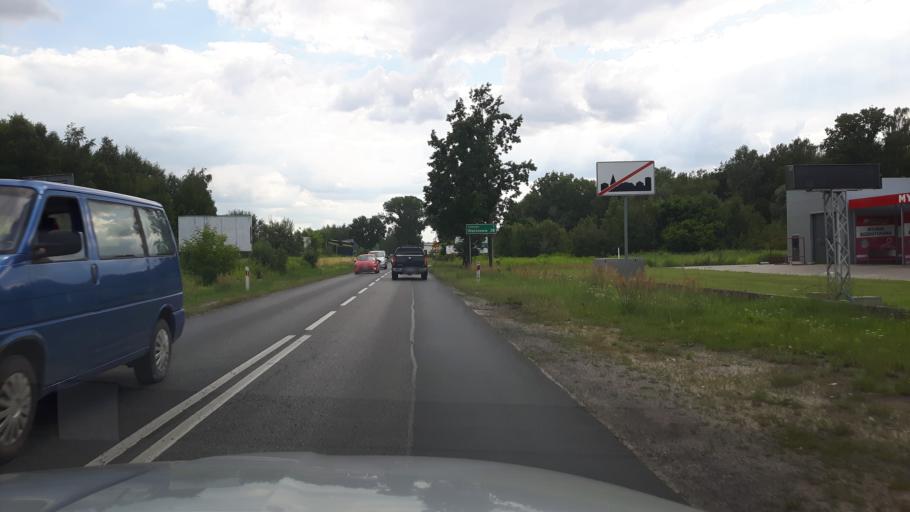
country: PL
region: Masovian Voivodeship
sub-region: Powiat wolominski
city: Kobylka
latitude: 52.3242
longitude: 21.2096
